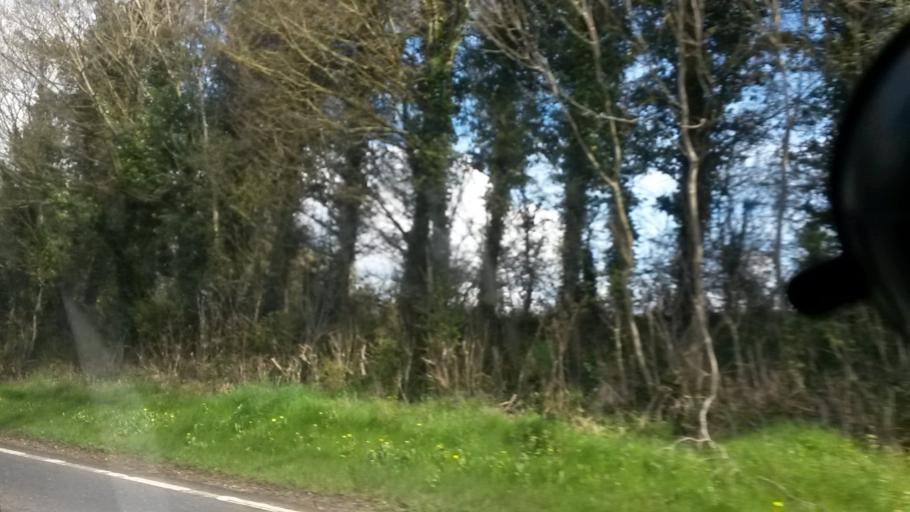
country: IE
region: Ulster
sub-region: An Cabhan
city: Belturbet
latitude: 54.1396
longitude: -7.5078
